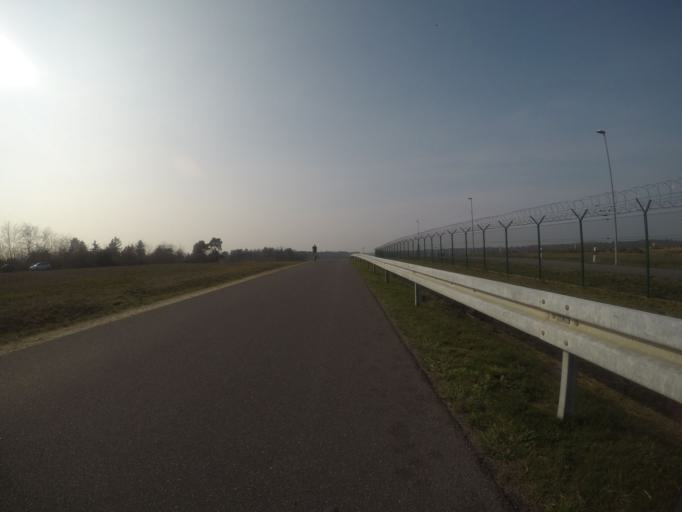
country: DE
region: Brandenburg
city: Rangsdorf
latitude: 52.3416
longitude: 13.4576
